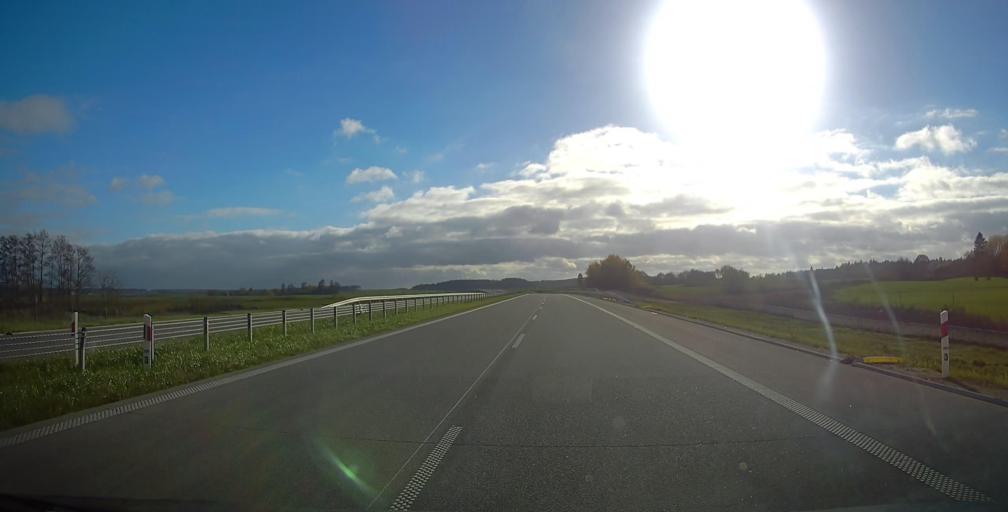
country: PL
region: Warmian-Masurian Voivodeship
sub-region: Powiat elcki
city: Elk
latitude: 53.7207
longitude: 22.2806
